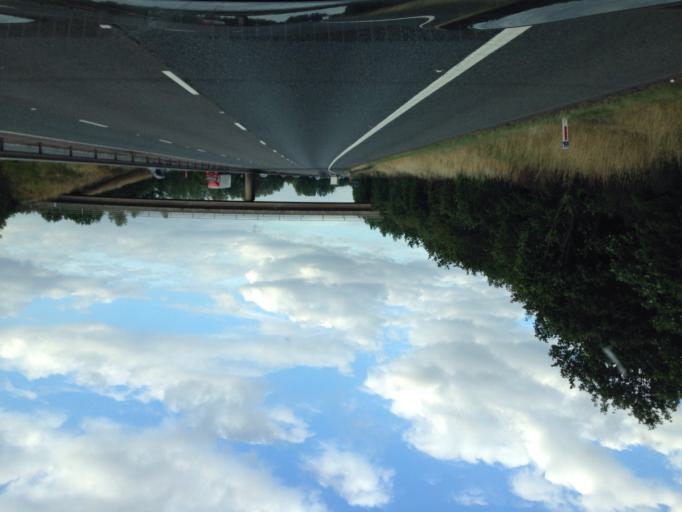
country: GB
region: England
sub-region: Oxfordshire
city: Bicester
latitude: 51.8513
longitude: -1.1728
